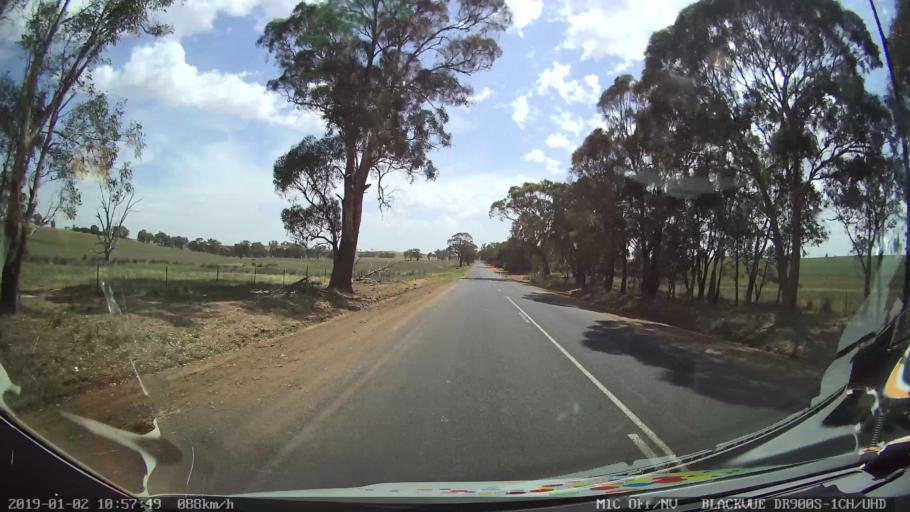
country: AU
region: New South Wales
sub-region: Cootamundra
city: Cootamundra
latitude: -34.6309
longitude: 148.2855
